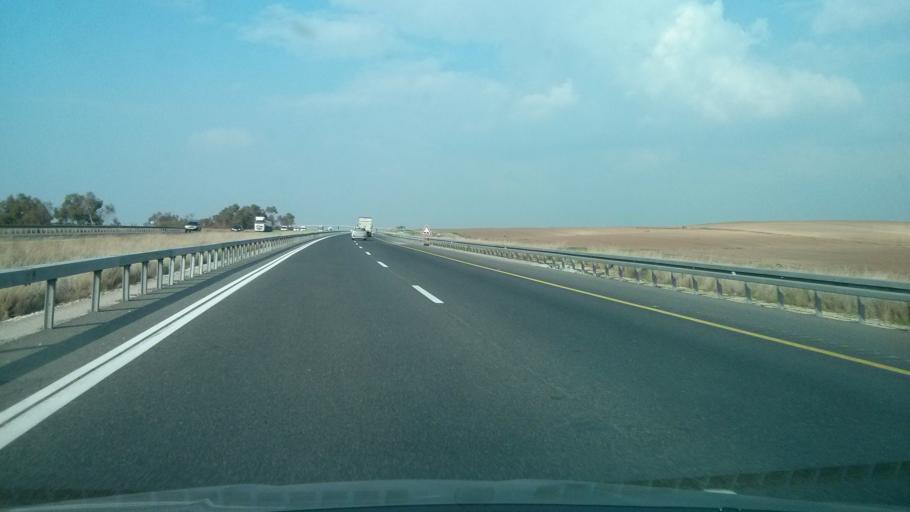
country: IL
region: Central District
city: Gedera
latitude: 31.7555
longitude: 34.8250
